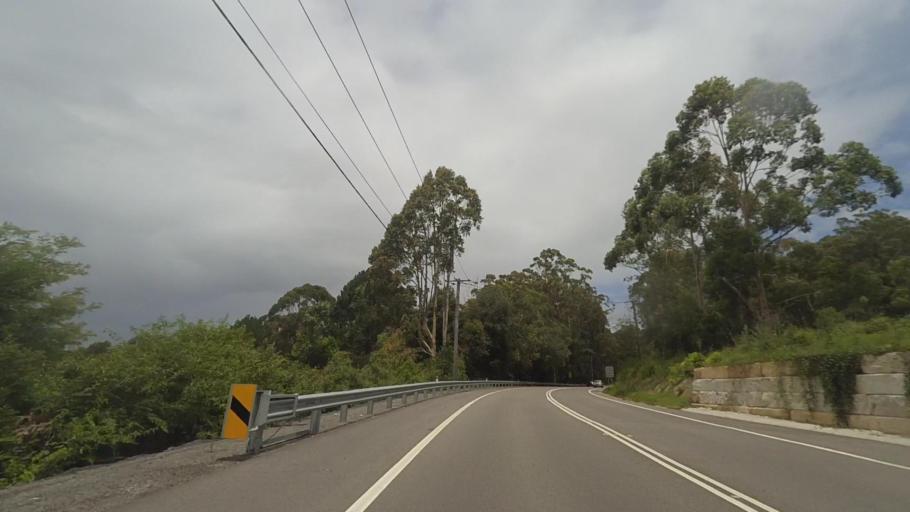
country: AU
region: New South Wales
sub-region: Wyong Shire
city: Chittaway Bay
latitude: -33.3342
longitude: 151.4125
